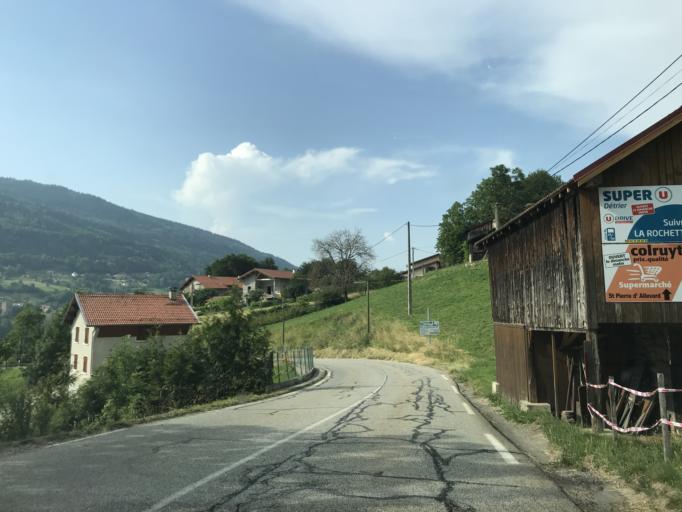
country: FR
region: Rhone-Alpes
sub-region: Departement de l'Isere
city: Allevard
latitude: 45.3934
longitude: 6.0798
